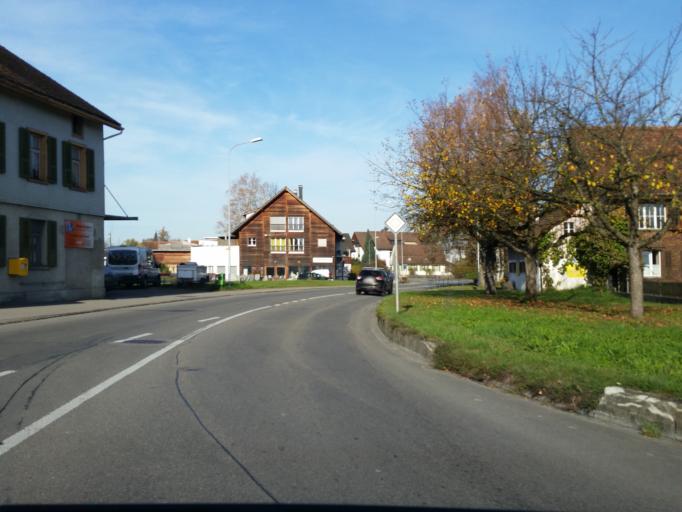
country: CH
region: Thurgau
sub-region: Arbon District
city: Amriswil
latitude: 47.5494
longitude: 9.2738
